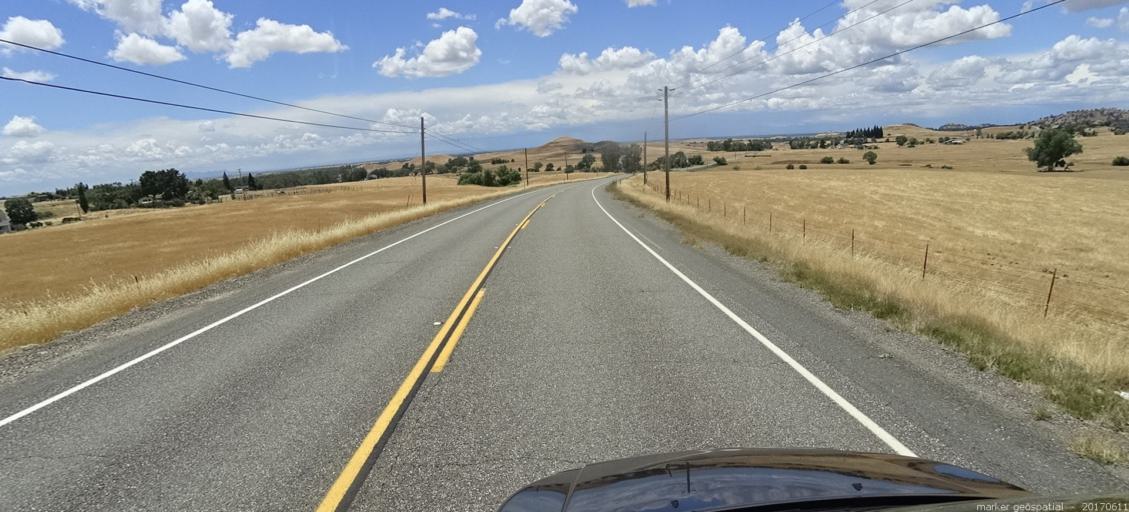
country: US
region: California
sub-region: Butte County
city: Paradise
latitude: 39.6489
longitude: -121.6039
